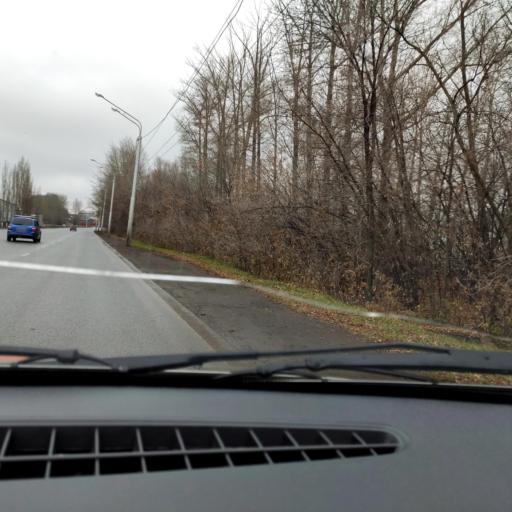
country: RU
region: Bashkortostan
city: Avdon
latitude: 54.6880
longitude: 55.8160
